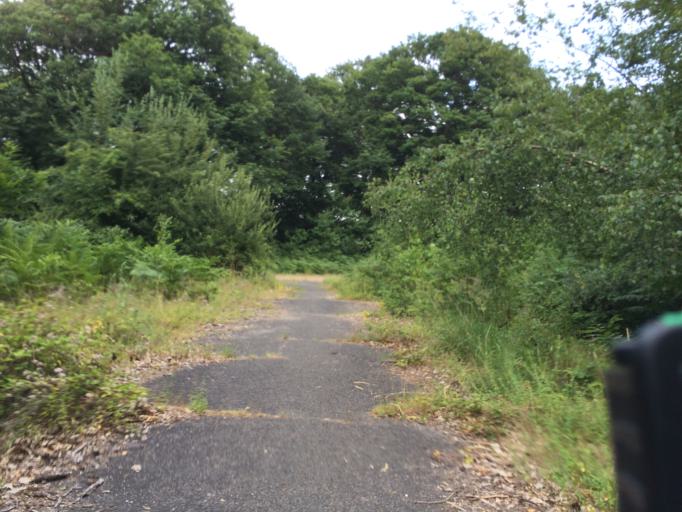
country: FR
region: Ile-de-France
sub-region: Departement de l'Essonne
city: Soisy-sur-Seine
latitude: 48.6693
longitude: 2.4436
